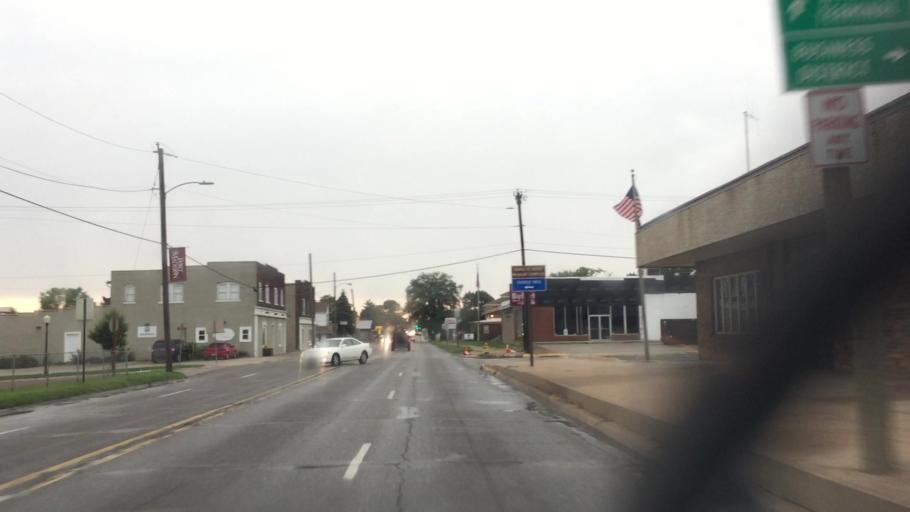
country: US
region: Iowa
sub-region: Lee County
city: Fort Madison
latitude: 40.6301
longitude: -91.3148
